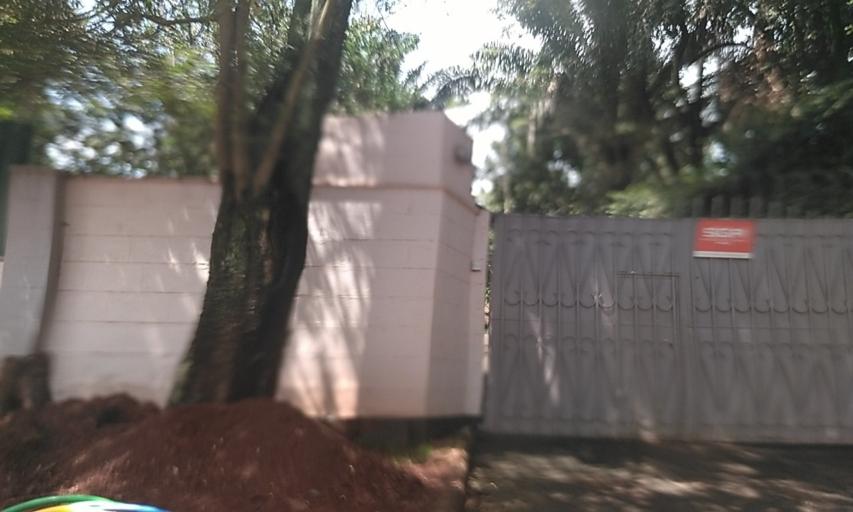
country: UG
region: Central Region
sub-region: Kampala District
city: Kampala
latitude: 0.3333
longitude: 32.6000
